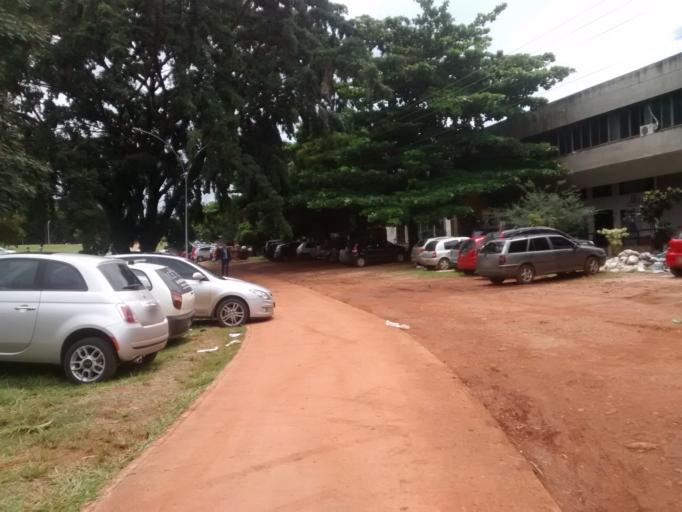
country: BR
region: Federal District
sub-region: Brasilia
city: Brasilia
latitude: -15.7843
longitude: -47.8779
